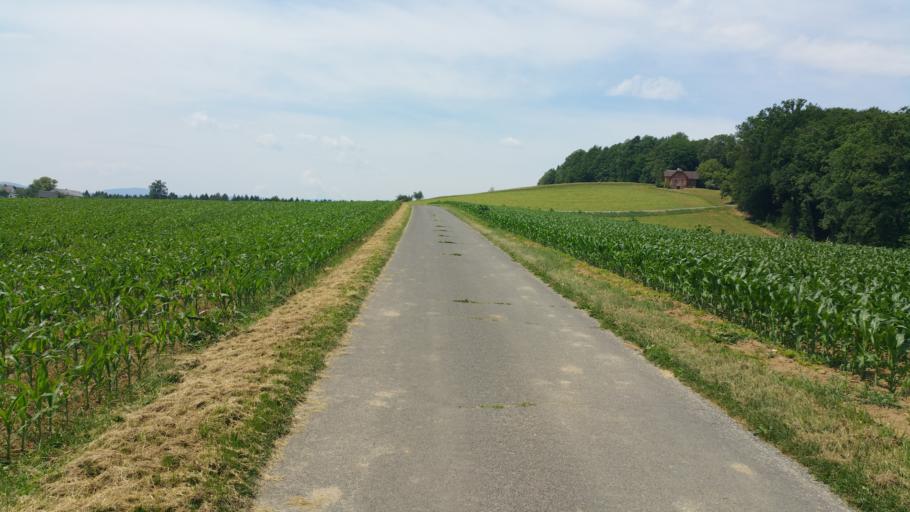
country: AT
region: Styria
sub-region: Politischer Bezirk Leibnitz
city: Pistorf
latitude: 46.7670
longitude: 15.3339
